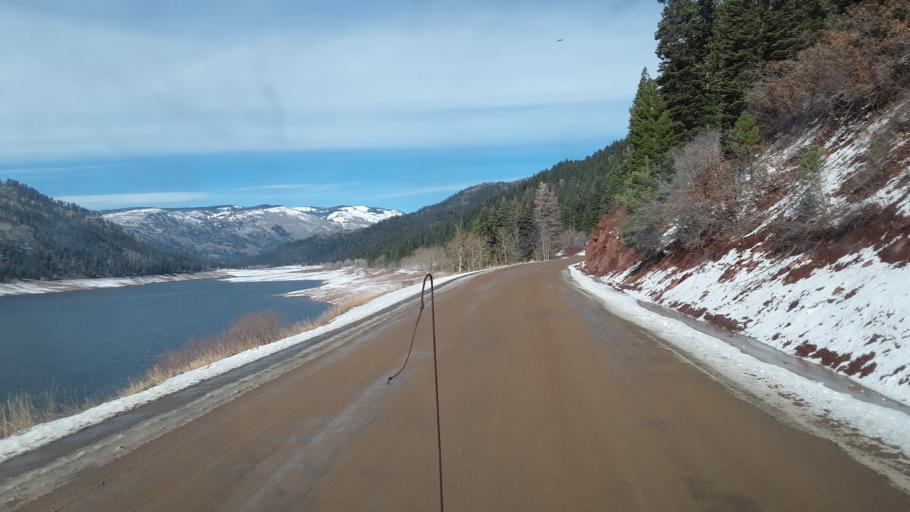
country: US
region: Colorado
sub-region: La Plata County
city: Bayfield
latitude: 37.3885
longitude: -107.6569
